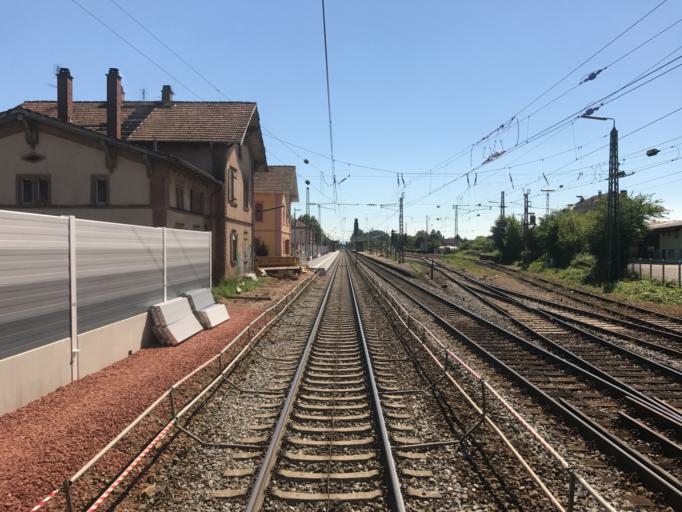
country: DE
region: Baden-Wuerttemberg
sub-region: Freiburg Region
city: Lahr
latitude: 48.3436
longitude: 7.8375
